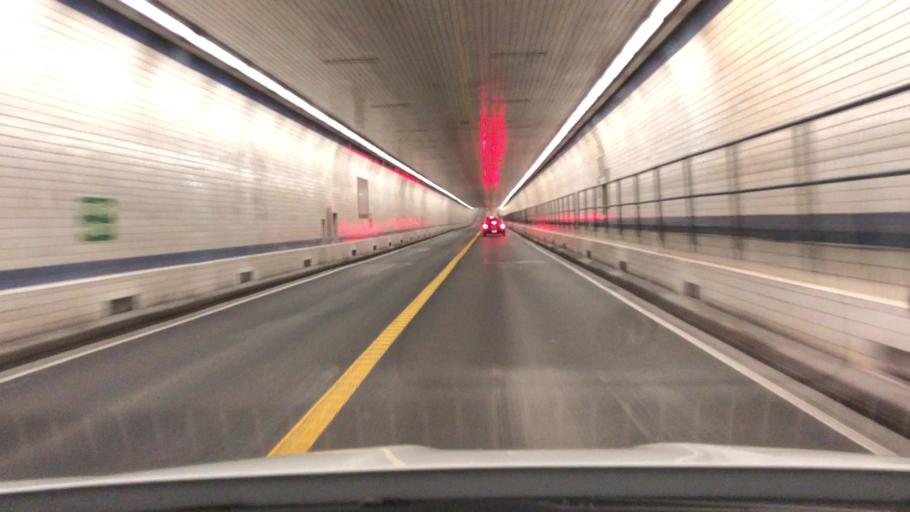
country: US
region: Virginia
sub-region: City of Virginia Beach
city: Virginia Beach
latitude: 37.0440
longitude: -76.0662
